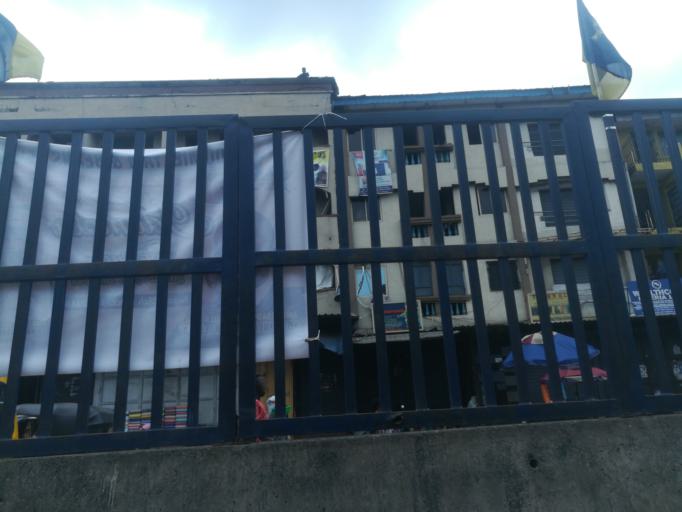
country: NG
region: Lagos
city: Lagos
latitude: 6.4621
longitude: 3.3869
